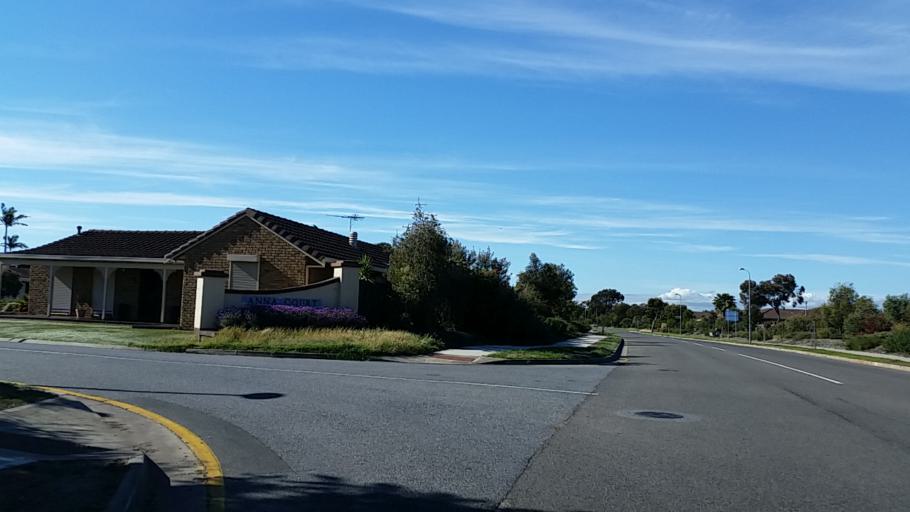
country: AU
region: South Australia
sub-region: Charles Sturt
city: West Lakes Shore
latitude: -34.8649
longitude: 138.4914
